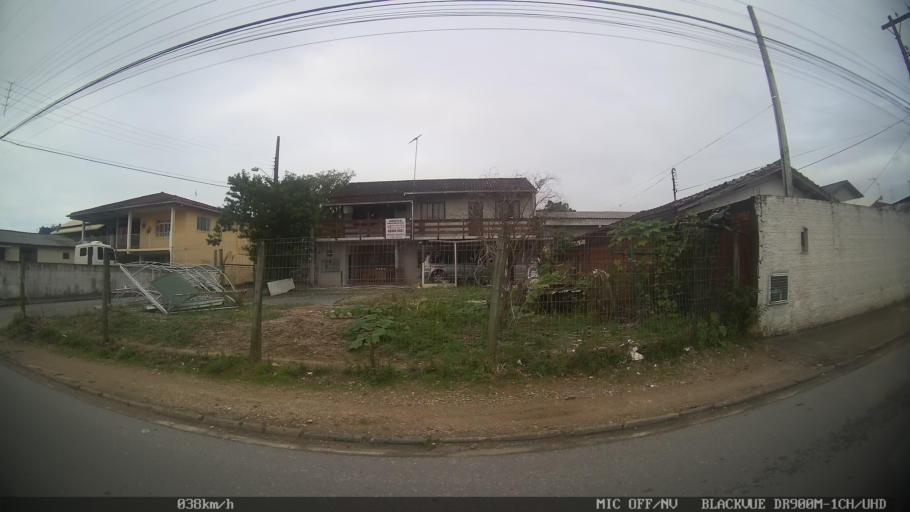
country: BR
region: Santa Catarina
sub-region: Biguacu
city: Biguacu
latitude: -27.5369
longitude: -48.6374
